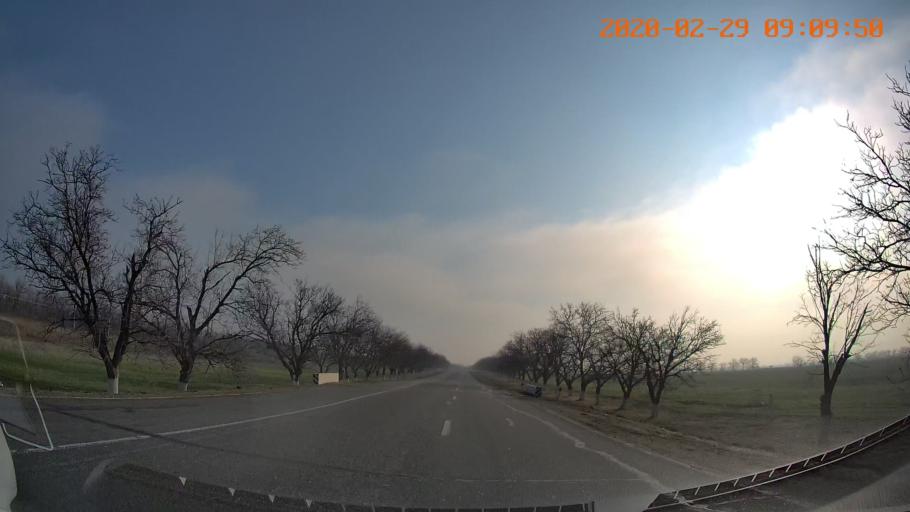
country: MD
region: Telenesti
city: Slobozia
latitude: 46.8449
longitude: 29.7698
